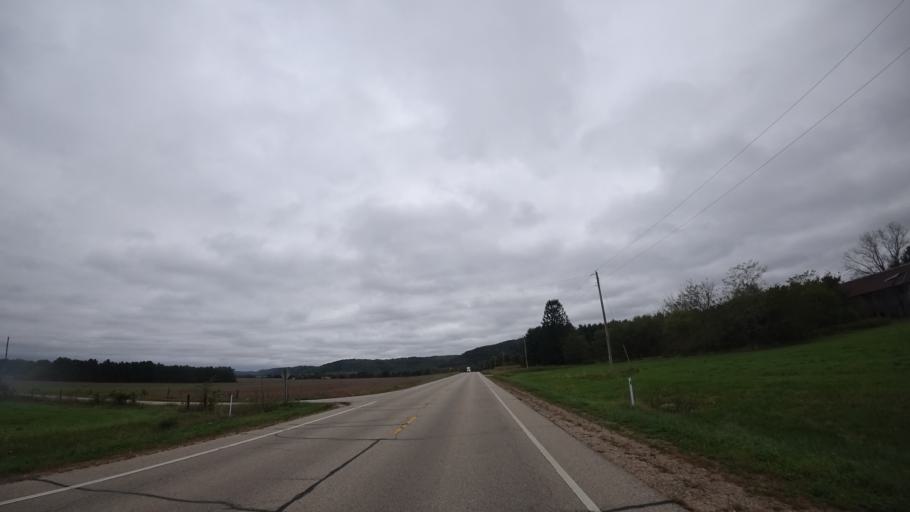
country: US
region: Wisconsin
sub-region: Grant County
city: Boscobel
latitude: 43.2053
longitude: -90.6267
